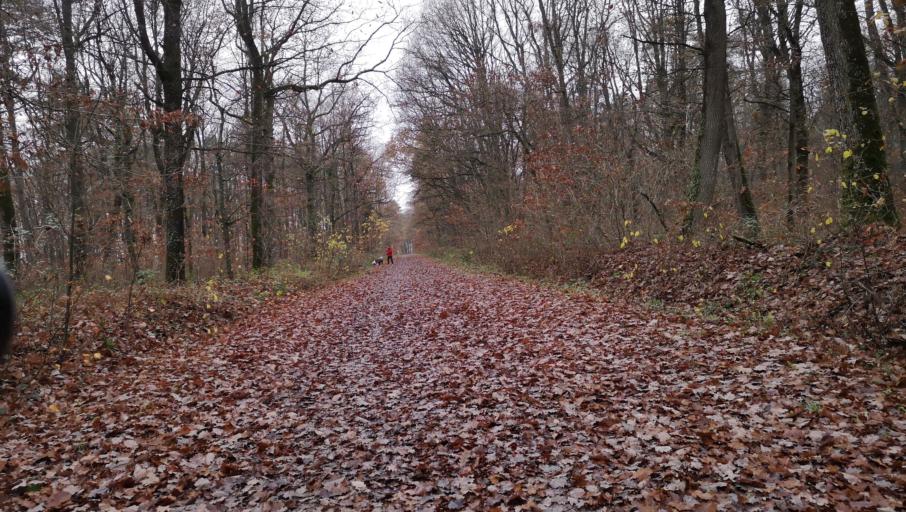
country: FR
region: Centre
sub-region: Departement du Loiret
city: Chanteau
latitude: 47.9413
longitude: 1.9745
